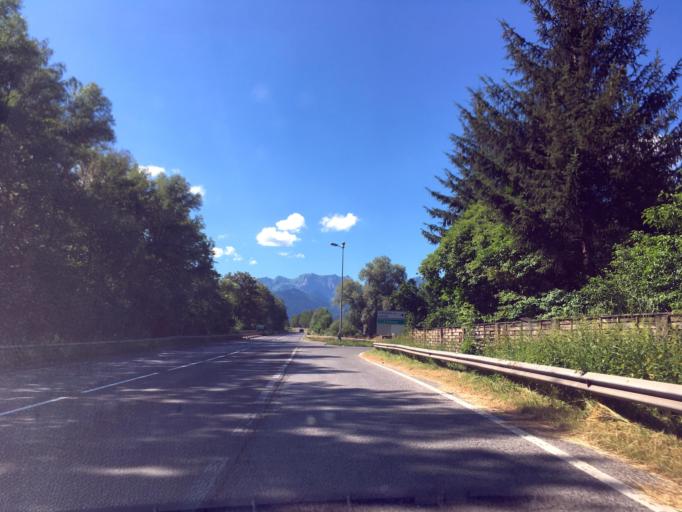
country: AT
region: Styria
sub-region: Politischer Bezirk Leoben
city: Sankt Peter-Freienstein
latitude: 47.4075
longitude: 15.0278
